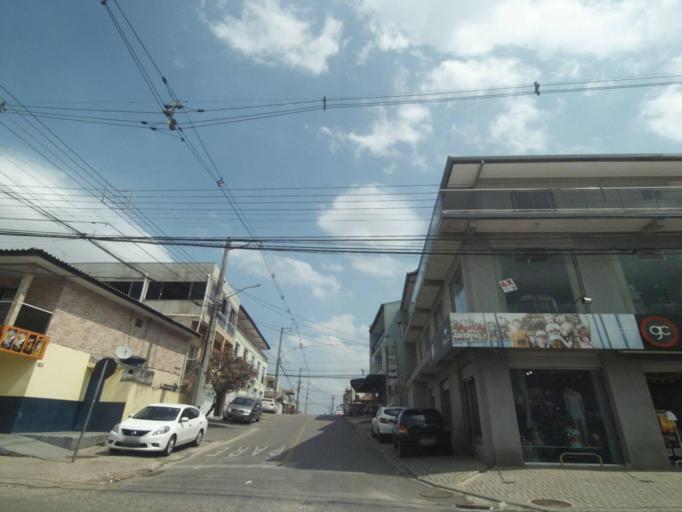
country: BR
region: Parana
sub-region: Curitiba
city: Curitiba
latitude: -25.4995
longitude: -49.3449
